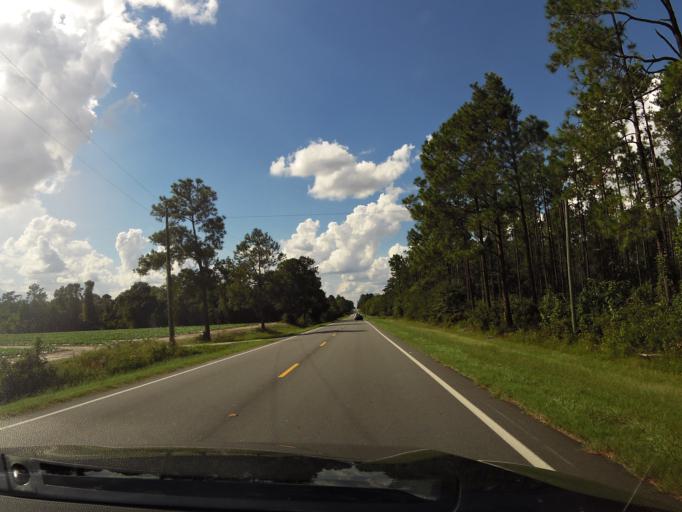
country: US
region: Georgia
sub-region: Echols County
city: Statenville
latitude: 30.7663
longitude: -83.1309
